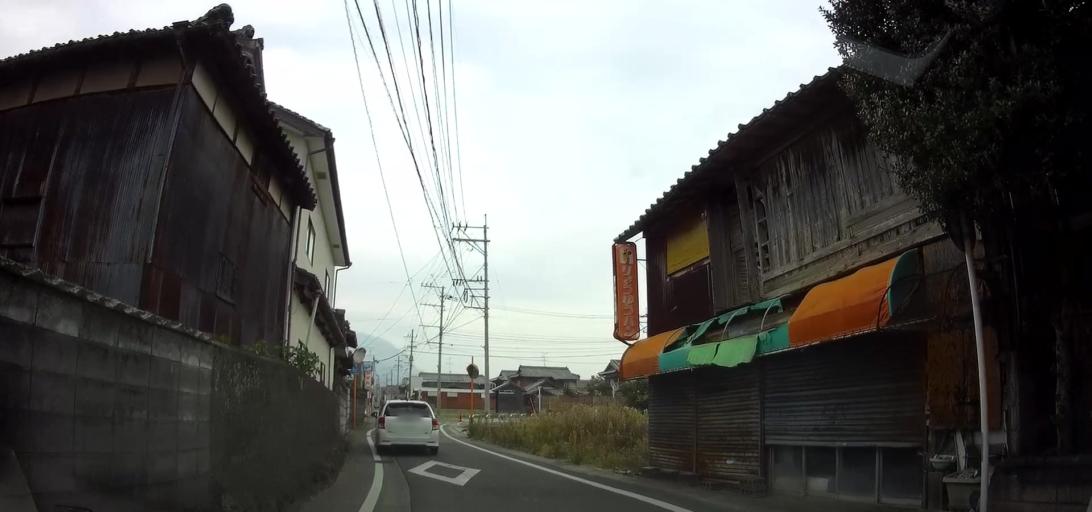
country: JP
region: Nagasaki
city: Shimabara
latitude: 32.6637
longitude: 130.3011
